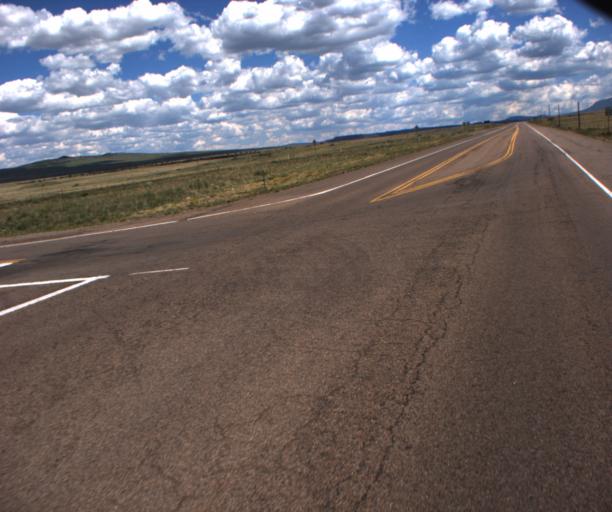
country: US
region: Arizona
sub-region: Apache County
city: Springerville
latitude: 34.1740
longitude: -109.3183
